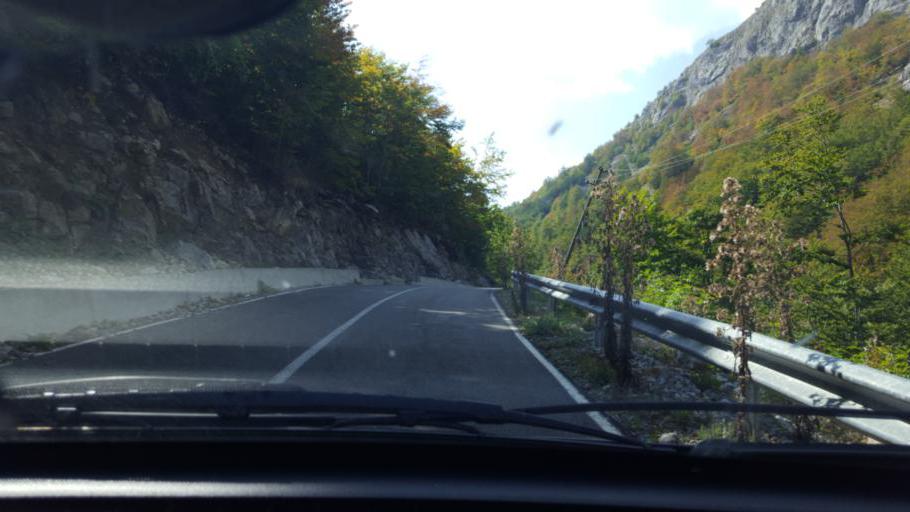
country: ME
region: Andrijevica
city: Andrijevica
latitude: 42.5644
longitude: 19.7349
